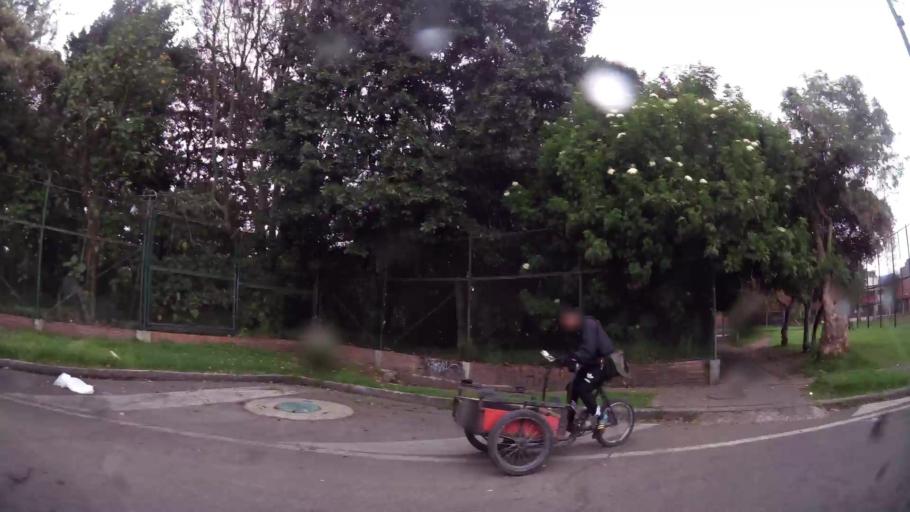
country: CO
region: Bogota D.C.
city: Barrio San Luis
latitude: 4.6926
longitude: -74.0950
